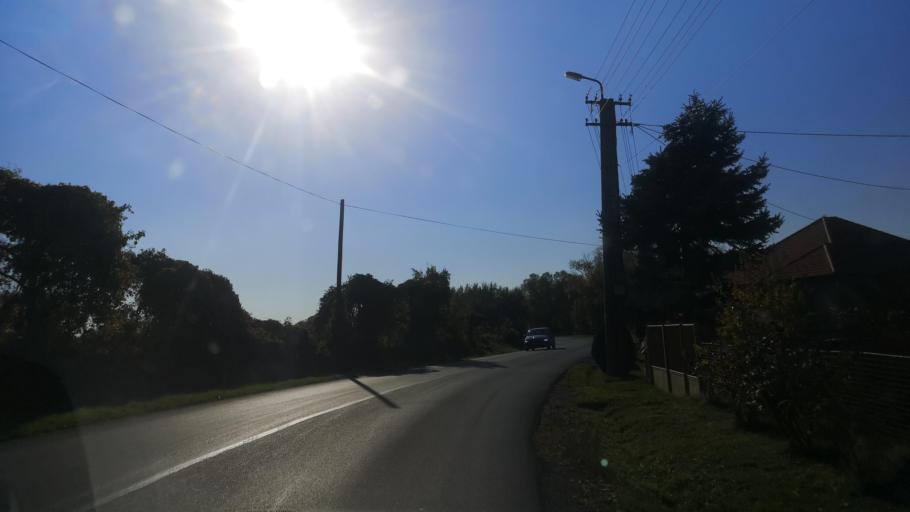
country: SK
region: Nitriansky
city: Zlate Moravce
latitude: 48.4447
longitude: 18.4343
